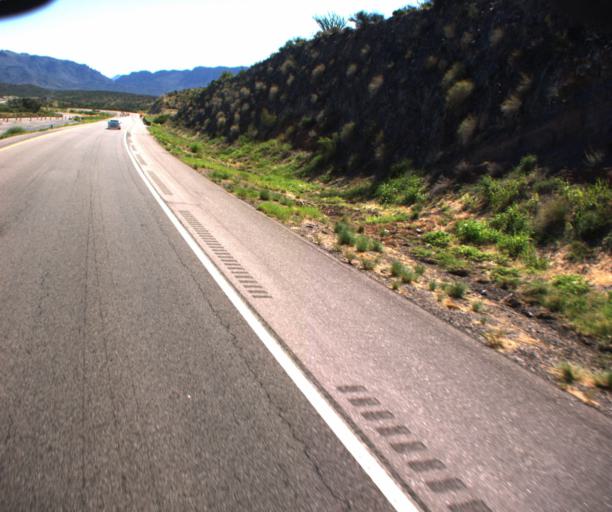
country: US
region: Arizona
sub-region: Pinal County
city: Superior
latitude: 33.2756
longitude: -111.1805
